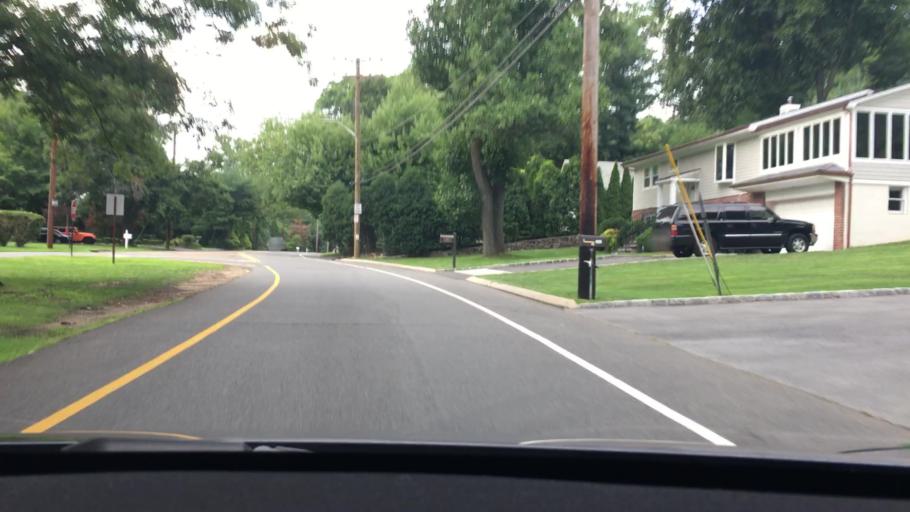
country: US
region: New York
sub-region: Westchester County
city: Larchmont
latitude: 40.9465
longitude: -73.7775
